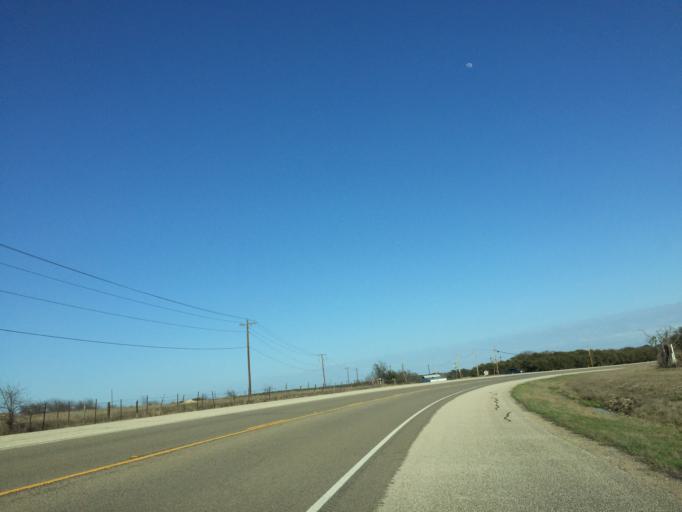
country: US
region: Texas
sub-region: Williamson County
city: Florence
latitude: 30.7721
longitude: -97.8190
